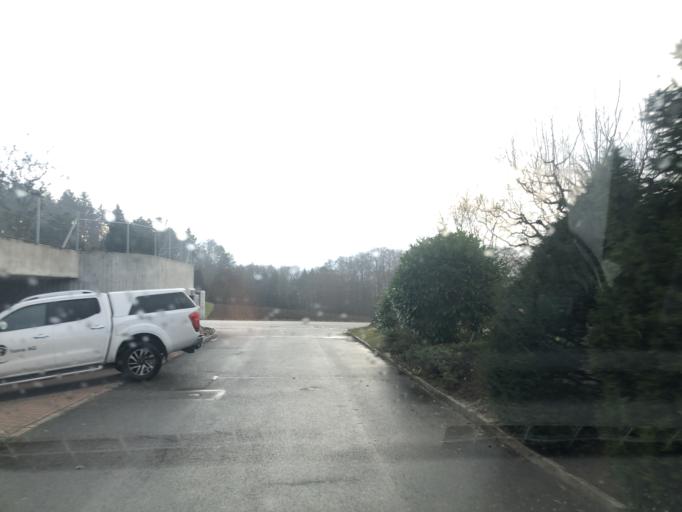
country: CH
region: Aargau
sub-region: Bezirk Baden
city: Kunten
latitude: 47.3842
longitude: 8.3310
